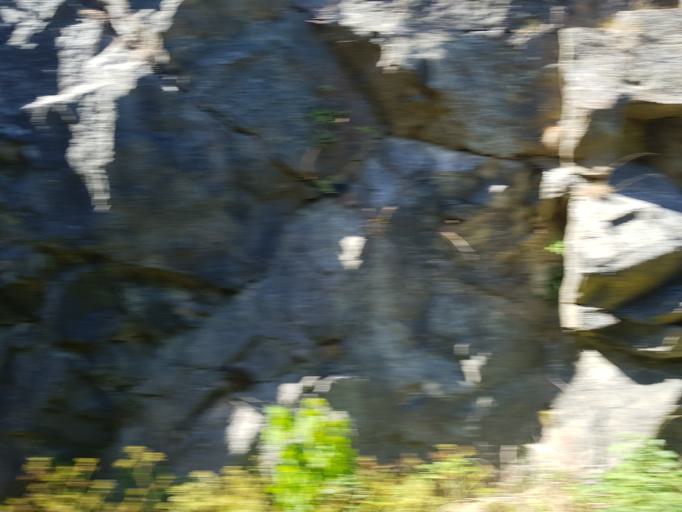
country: SE
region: Vaestra Goetaland
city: Ronnang
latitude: 57.9460
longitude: 11.6082
